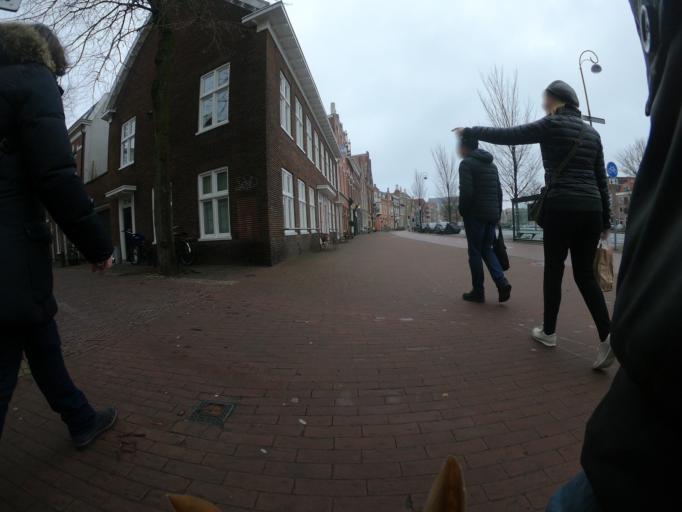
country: NL
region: North Holland
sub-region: Gemeente Haarlem
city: Haarlem
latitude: 52.3772
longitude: 4.6383
